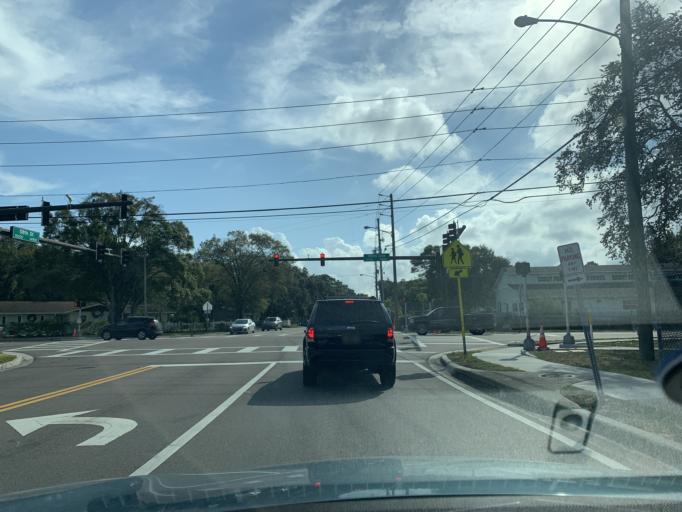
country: US
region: Florida
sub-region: Pinellas County
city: South Highpoint
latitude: 27.9090
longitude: -82.7129
